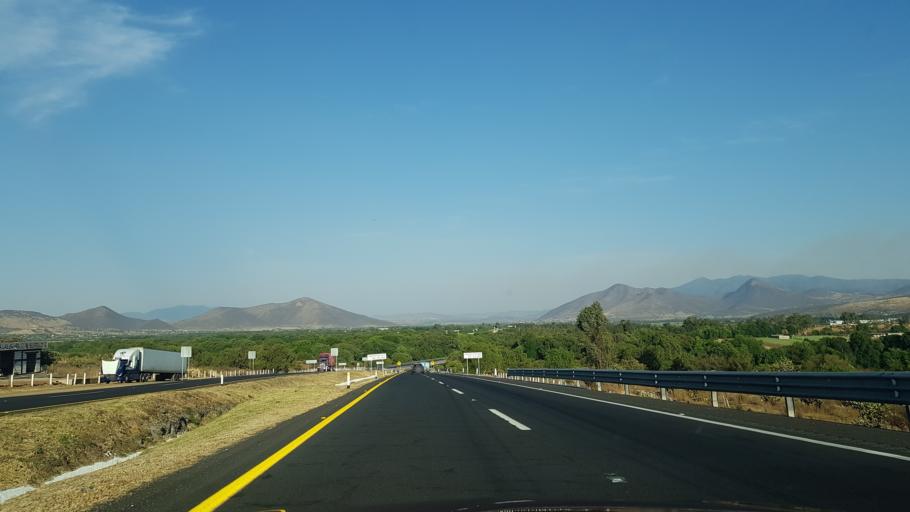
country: MX
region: Michoacan
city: Maravatio
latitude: 19.9051
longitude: -100.4261
